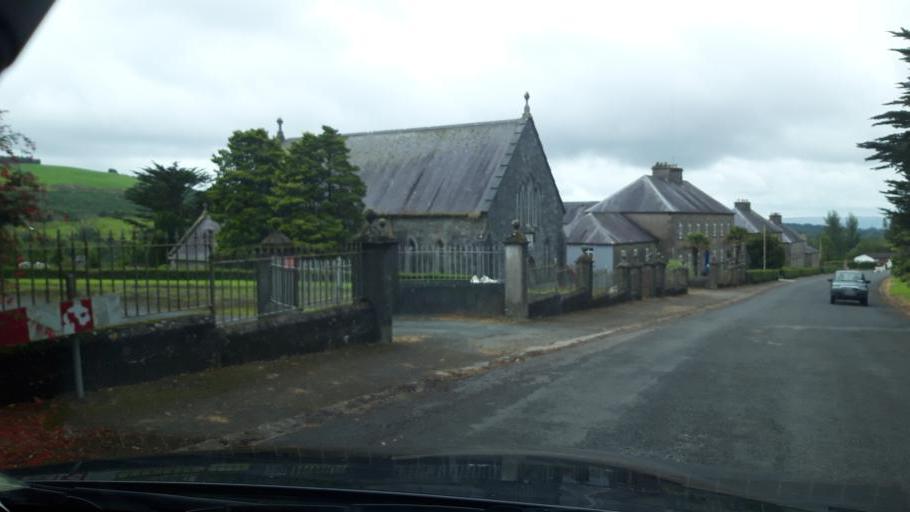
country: IE
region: Munster
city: Cahir
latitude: 52.1851
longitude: -7.8496
